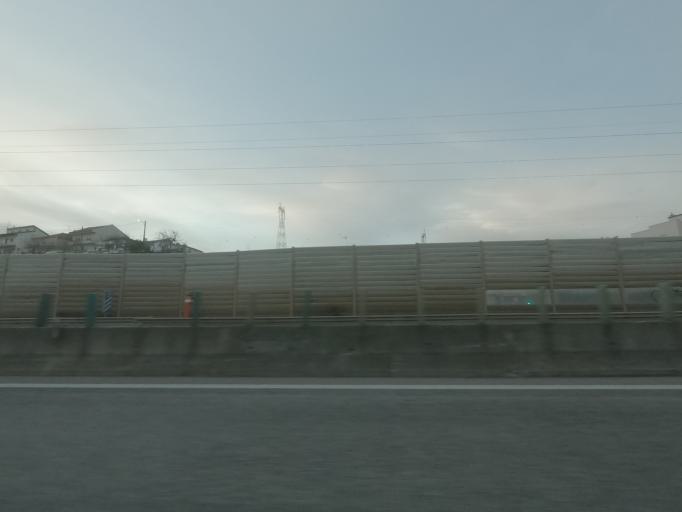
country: PT
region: Lisbon
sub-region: Vila Franca de Xira
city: Sobralinho
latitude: 38.9027
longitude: -9.0430
